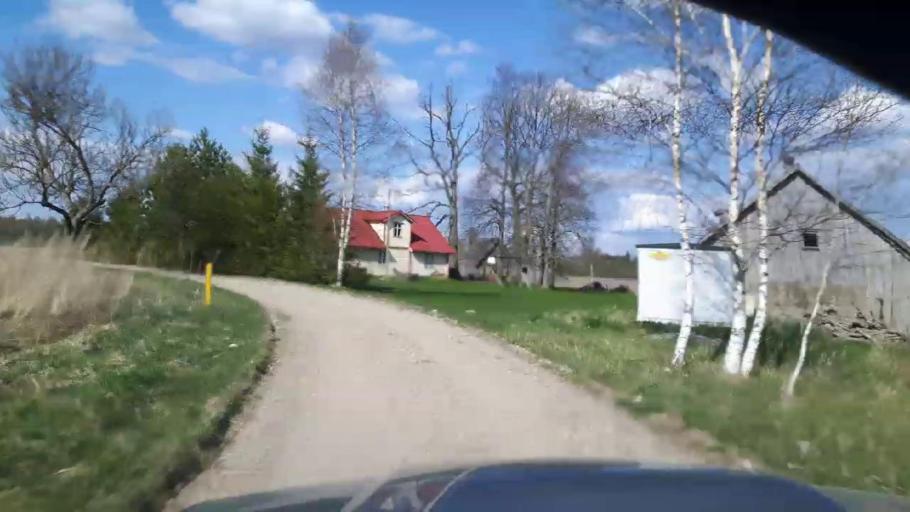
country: EE
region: Paernumaa
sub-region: Tootsi vald
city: Tootsi
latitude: 58.4378
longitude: 24.8724
